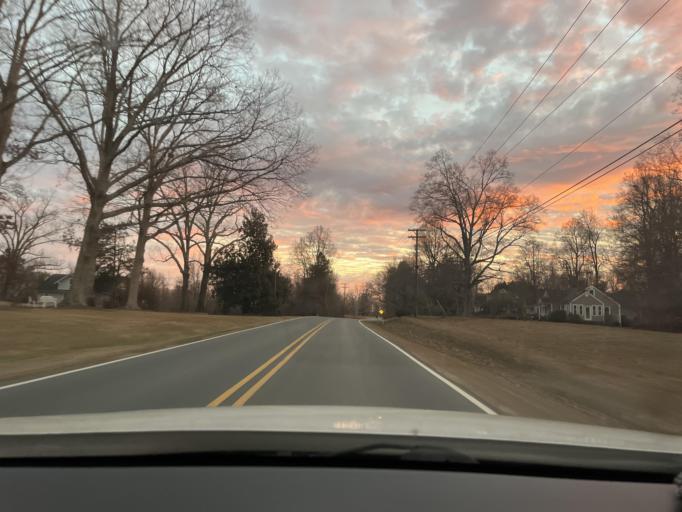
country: US
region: North Carolina
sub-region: Guilford County
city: Forest Oaks
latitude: 36.0209
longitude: -79.7269
